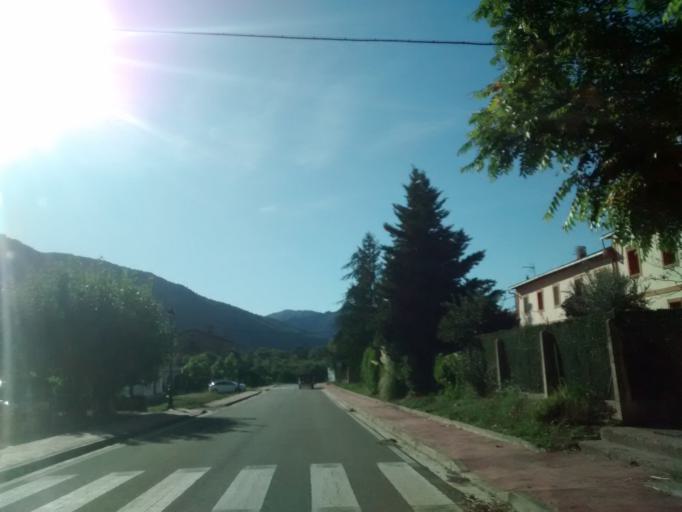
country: ES
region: Aragon
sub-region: Provincia de Huesca
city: Loarre
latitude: 42.3819
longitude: -0.6968
